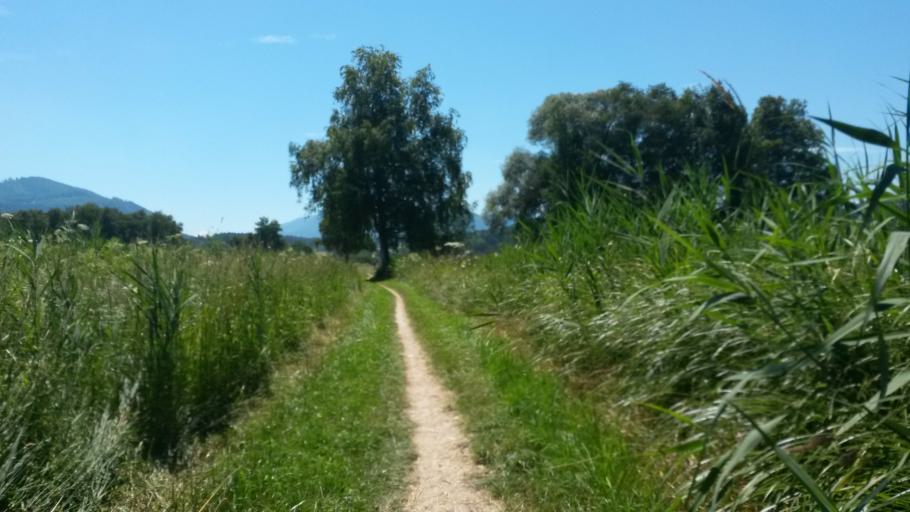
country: DE
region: Bavaria
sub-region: Upper Bavaria
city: Bernau am Chiemsee
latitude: 47.8259
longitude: 12.3731
